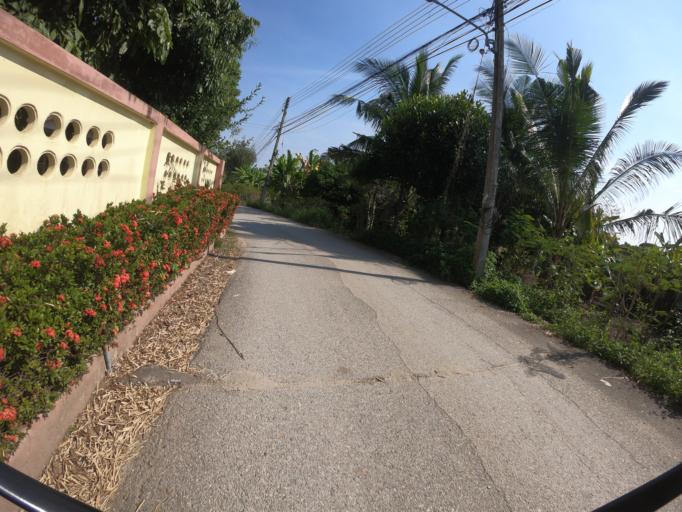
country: TH
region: Chiang Mai
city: San Sai
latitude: 18.8507
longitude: 98.9988
